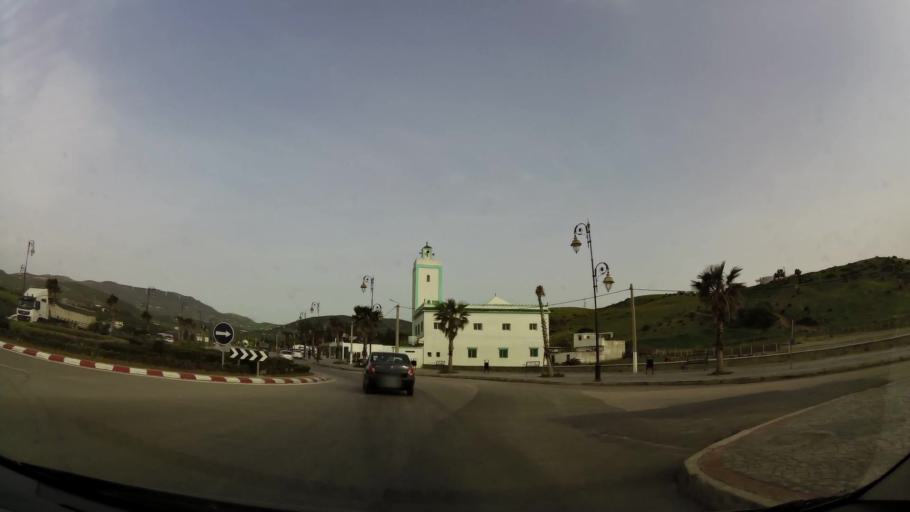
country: MA
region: Tanger-Tetouan
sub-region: Tanger-Assilah
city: Dar Chaoui
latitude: 35.5683
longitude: -5.6171
